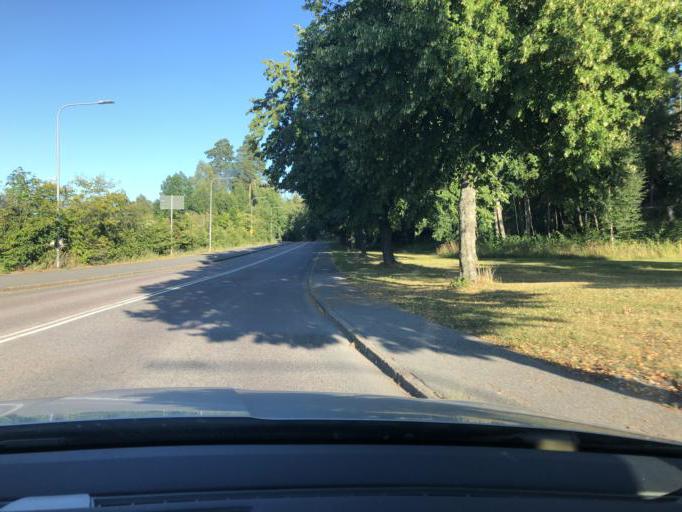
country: SE
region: Stockholm
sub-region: Sodertalje Kommun
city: Soedertaelje
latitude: 59.1821
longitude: 17.6176
